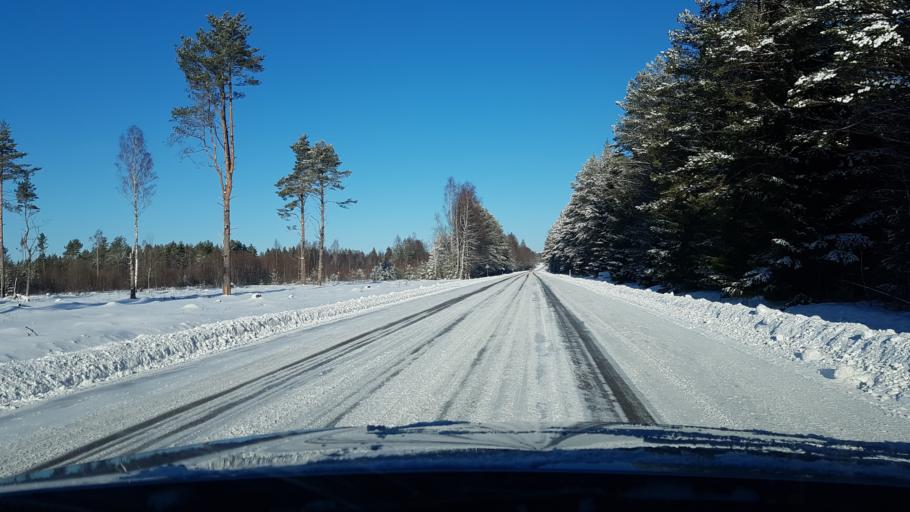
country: EE
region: Hiiumaa
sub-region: Kaerdla linn
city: Kardla
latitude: 58.9090
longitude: 22.7918
